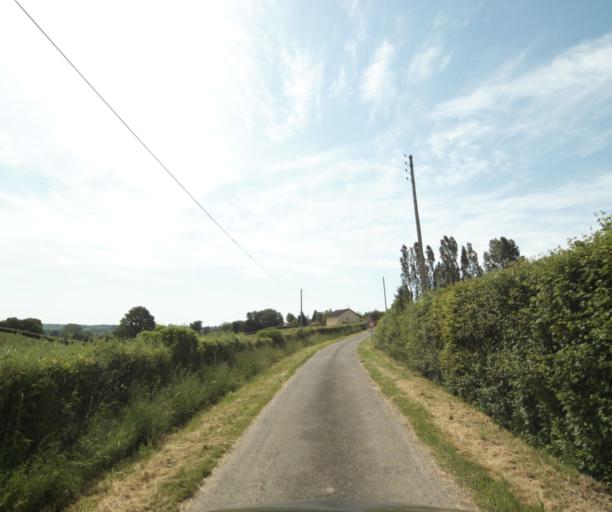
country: FR
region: Bourgogne
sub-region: Departement de Saone-et-Loire
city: Paray-le-Monial
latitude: 46.5397
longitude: 4.1250
